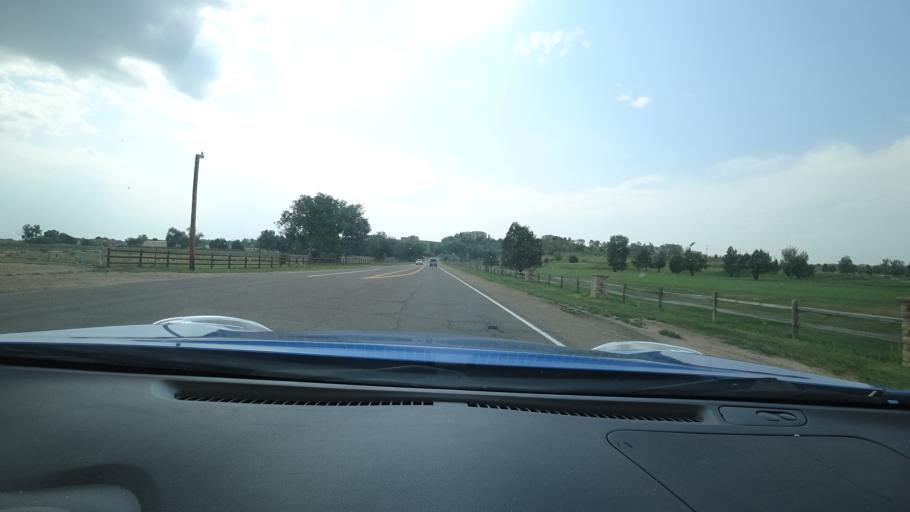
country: US
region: Colorado
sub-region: Adams County
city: Todd Creek
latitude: 39.9251
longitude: -104.8795
